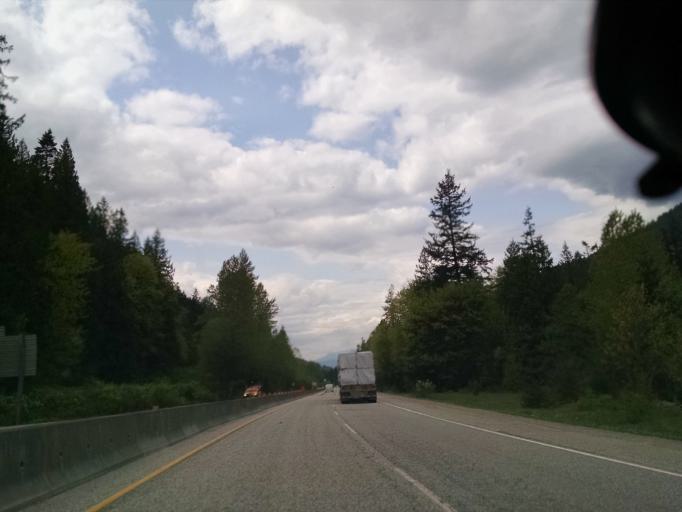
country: CA
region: British Columbia
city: Hope
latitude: 49.3788
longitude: -121.3242
